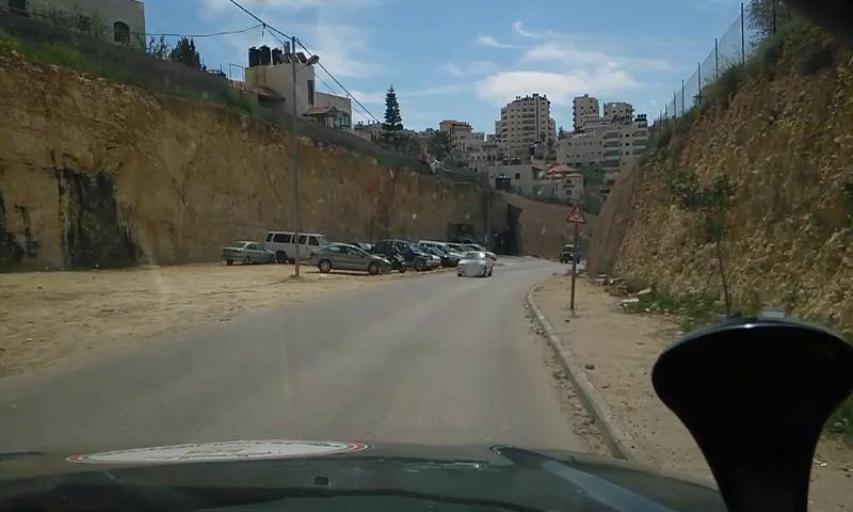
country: PS
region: West Bank
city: Bir Nabala
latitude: 31.8529
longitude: 35.2020
